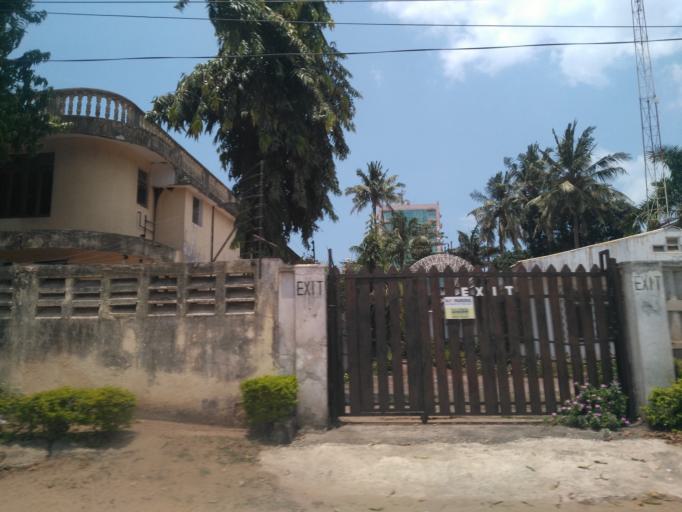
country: TZ
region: Dar es Salaam
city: Dar es Salaam
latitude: -6.8031
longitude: 39.2810
